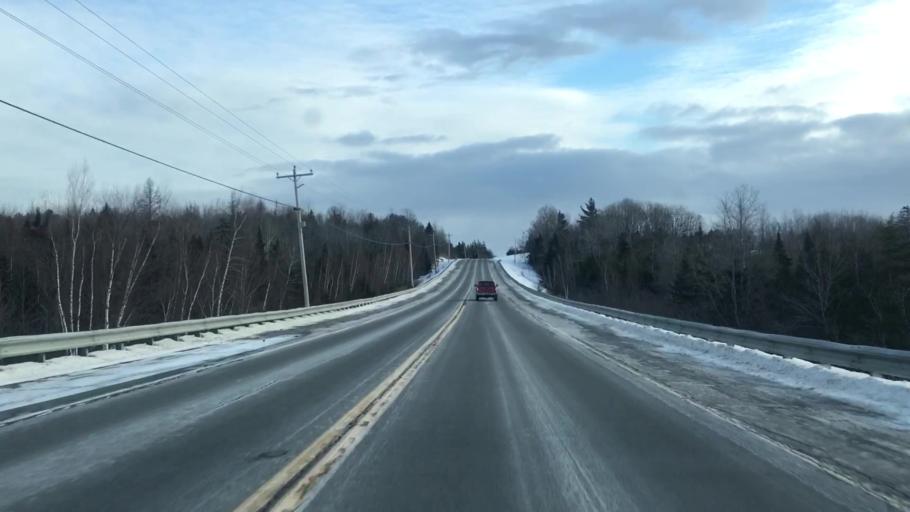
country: US
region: Maine
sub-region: Washington County
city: Calais
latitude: 45.0638
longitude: -67.5341
